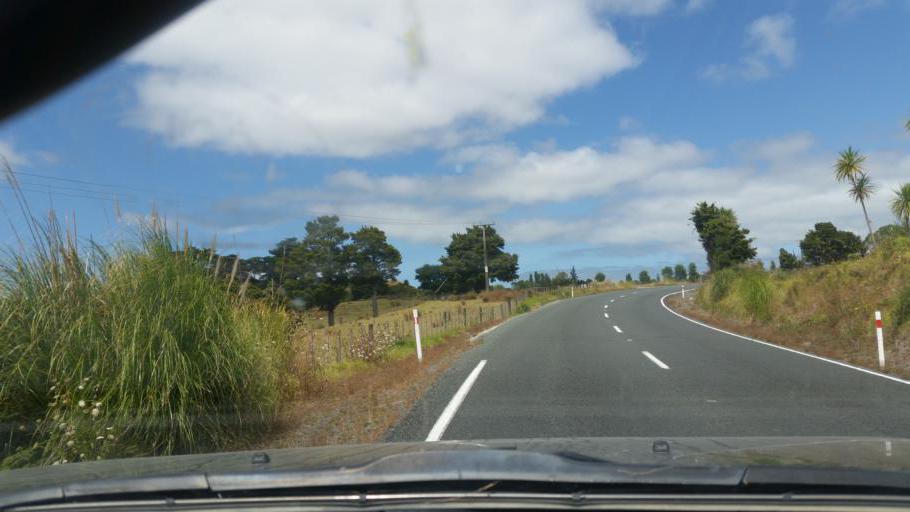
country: NZ
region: Auckland
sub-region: Auckland
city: Wellsford
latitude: -36.1353
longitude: 174.3239
